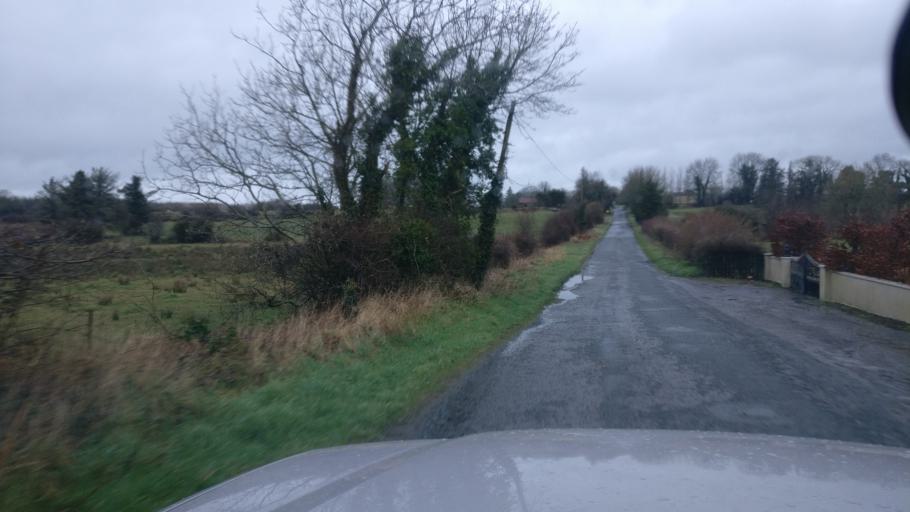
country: IE
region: Connaught
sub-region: County Galway
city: Ballinasloe
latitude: 53.2496
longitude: -8.3565
